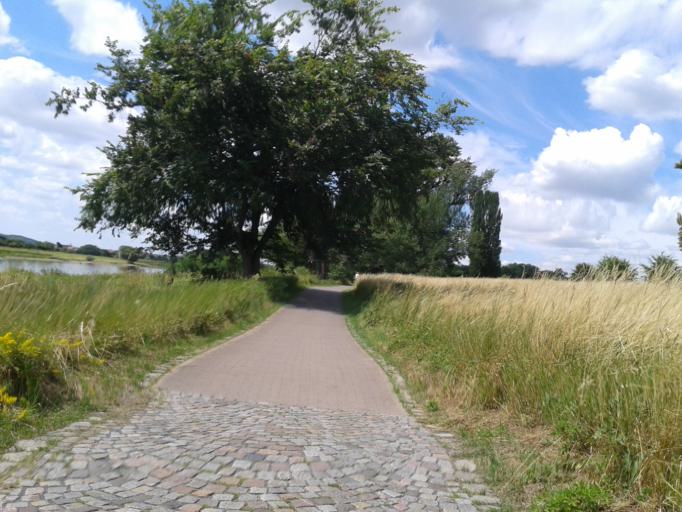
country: DE
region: Saxony
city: Radebeul
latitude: 51.0929
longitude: 13.6559
